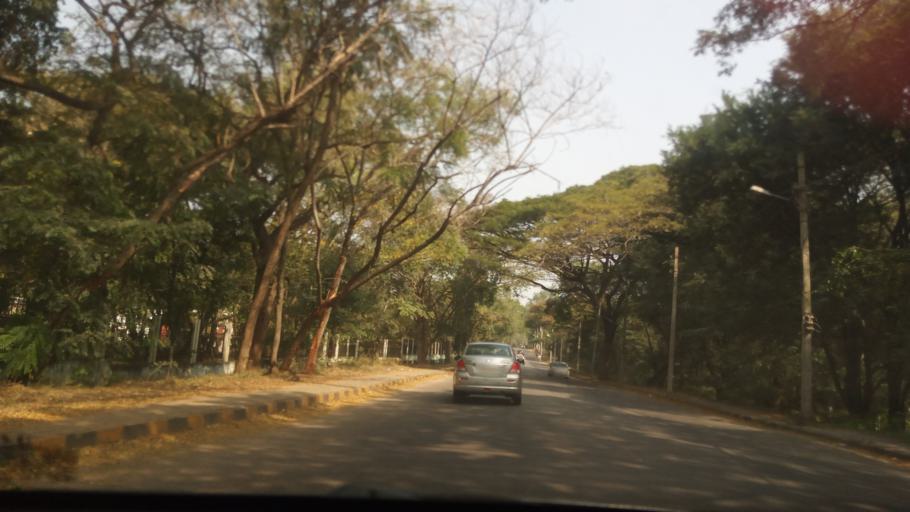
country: IN
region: Karnataka
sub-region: Mysore
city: Mysore
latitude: 12.3084
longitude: 76.6261
